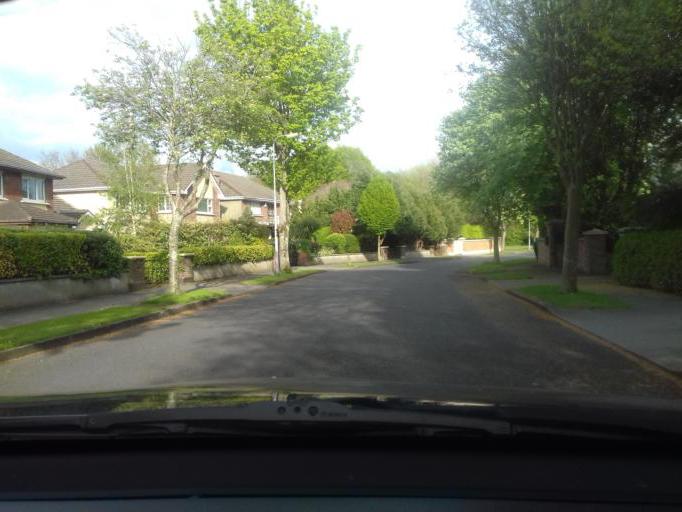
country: IE
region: Leinster
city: Castleknock
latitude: 53.3738
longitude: -6.3504
